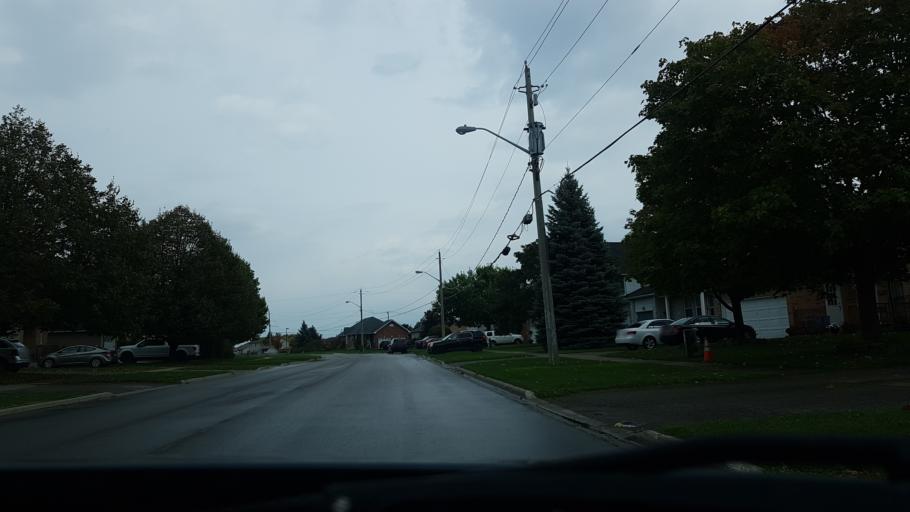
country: CA
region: Ontario
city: Omemee
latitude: 44.3693
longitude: -78.7464
